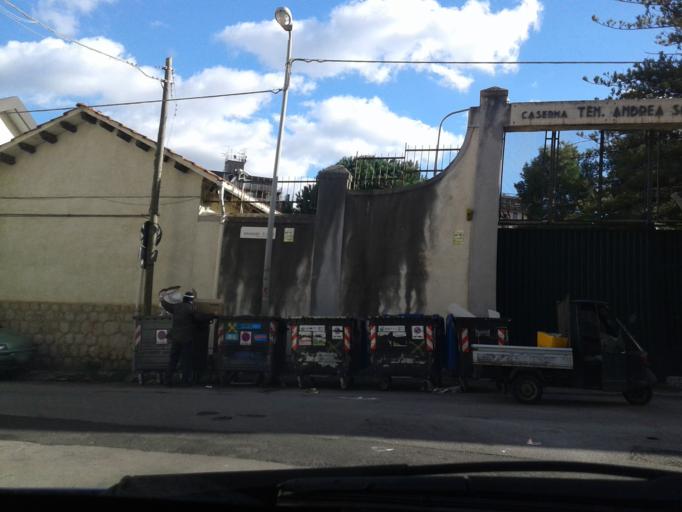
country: IT
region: Sicily
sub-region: Palermo
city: Palermo
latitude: 38.1053
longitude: 13.3411
